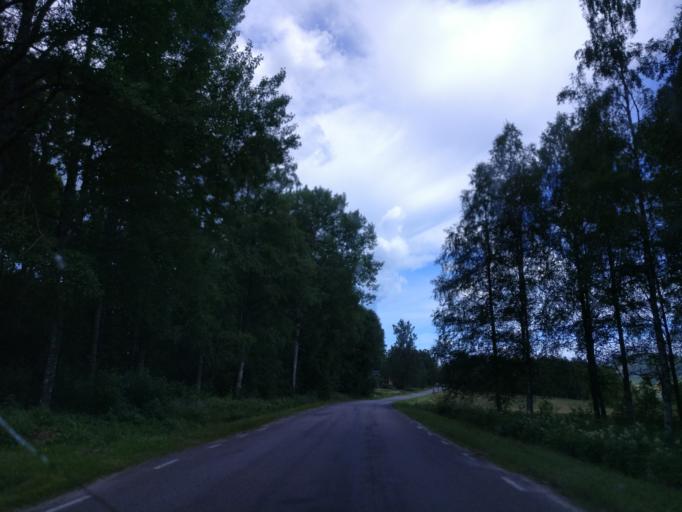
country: SE
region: Vaermland
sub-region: Hagfors Kommun
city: Ekshaerad
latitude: 60.1337
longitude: 13.4580
